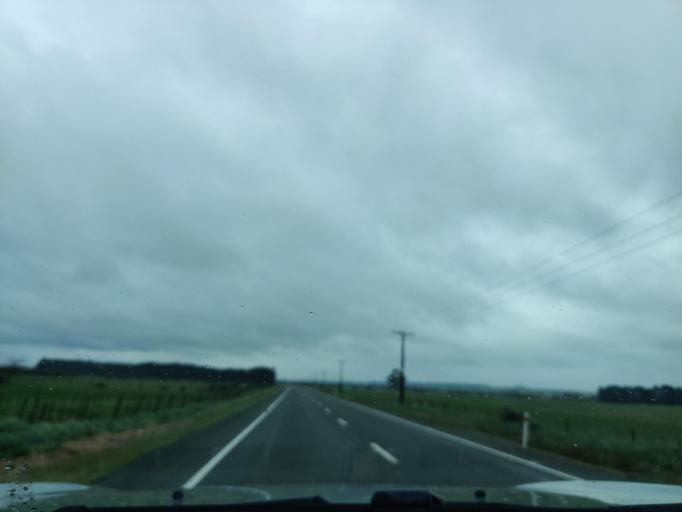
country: NZ
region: Hawke's Bay
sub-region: Hastings District
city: Hastings
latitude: -40.0112
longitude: 176.3757
